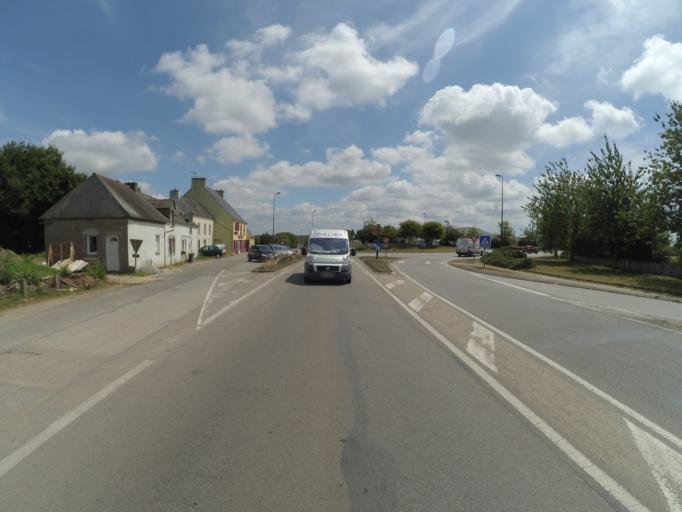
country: FR
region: Brittany
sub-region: Departement du Finistere
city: Ergue-Gaberic
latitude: 47.9757
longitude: -4.0007
